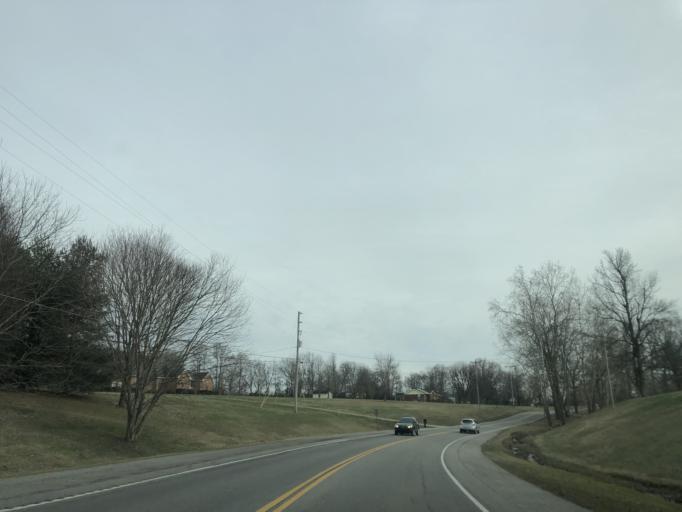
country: US
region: Tennessee
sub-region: Sumner County
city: White House
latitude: 36.4910
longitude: -86.5875
